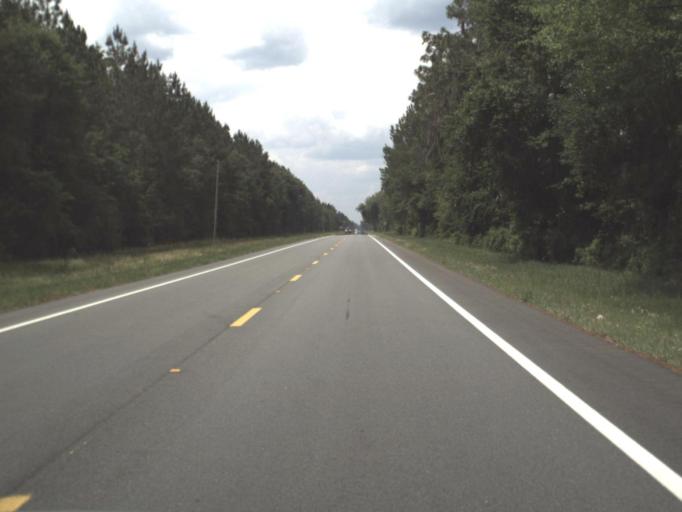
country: US
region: Florida
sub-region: Columbia County
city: Five Points
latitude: 30.4805
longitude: -82.6588
